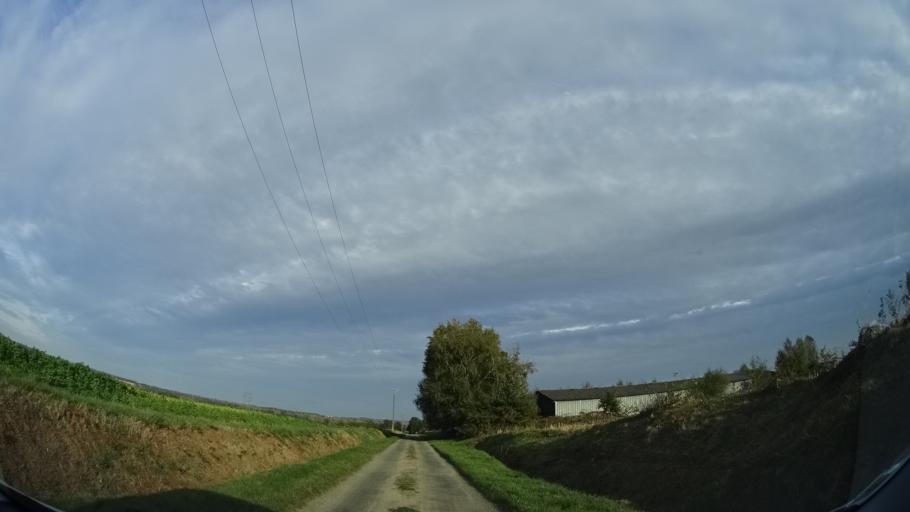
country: FR
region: Brittany
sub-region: Departement d'Ille-et-Vilaine
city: Geveze
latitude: 48.1954
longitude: -1.8005
